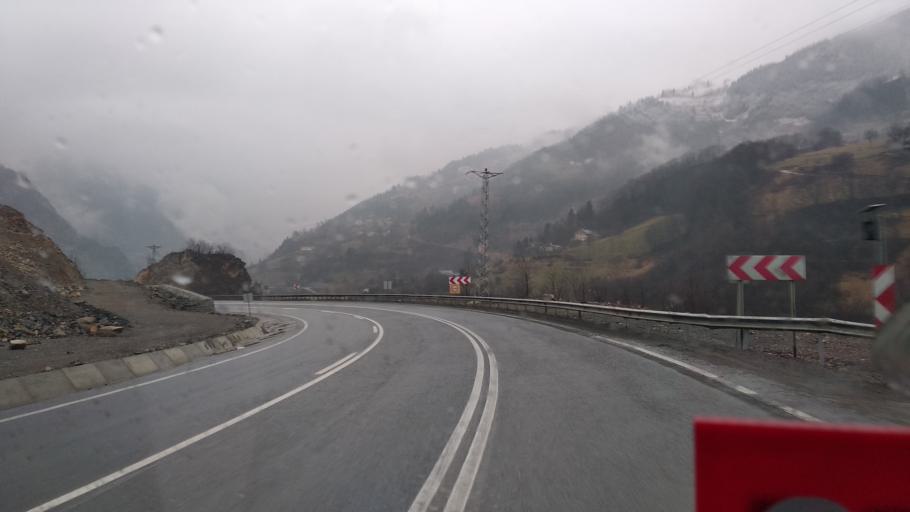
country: TR
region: Trabzon
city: Macka
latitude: 40.7136
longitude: 39.5138
